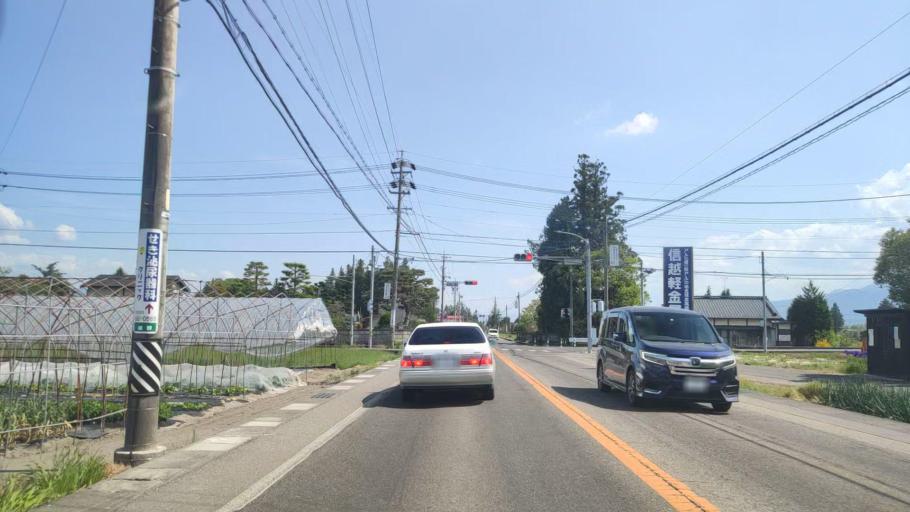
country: JP
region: Nagano
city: Hotaka
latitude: 36.3976
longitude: 137.8624
